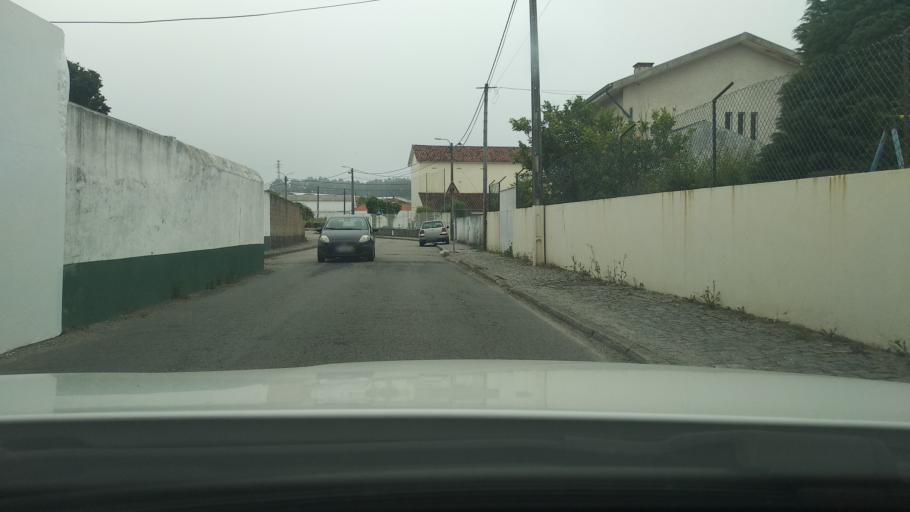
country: PT
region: Aveiro
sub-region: Espinho
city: Souto
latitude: 40.9883
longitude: -8.6249
